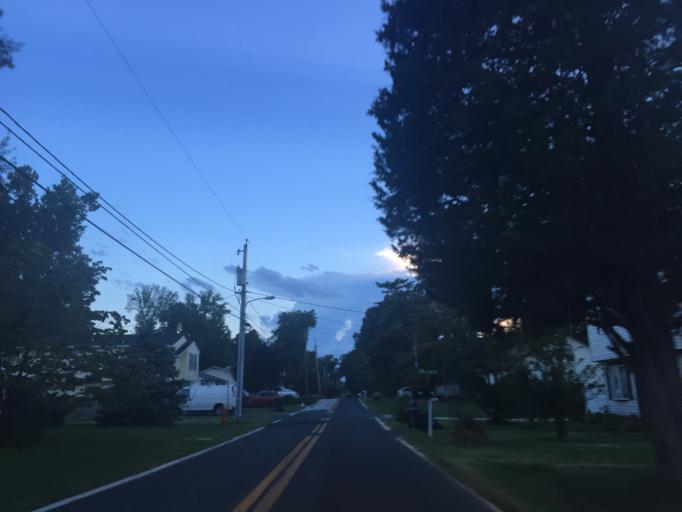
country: US
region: Maryland
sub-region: Baltimore County
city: Bowleys Quarters
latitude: 39.3768
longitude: -76.3547
